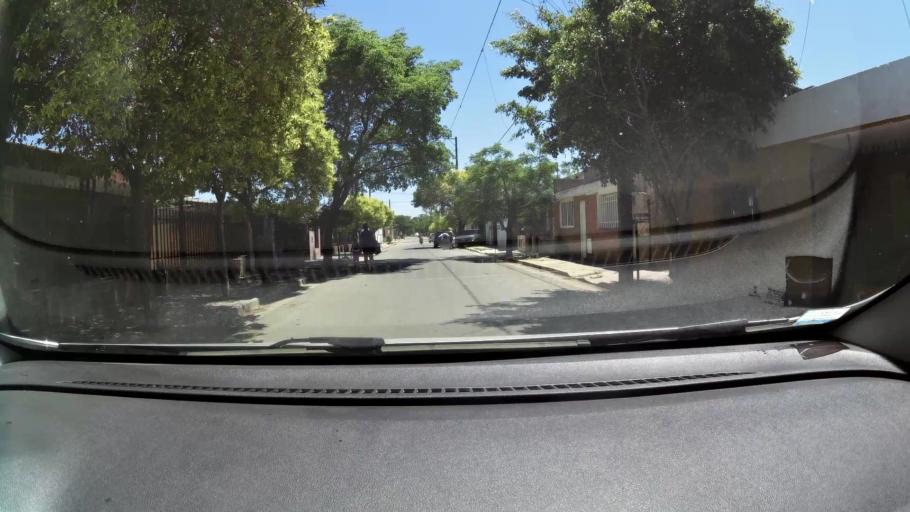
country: AR
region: Cordoba
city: Malvinas Argentinas
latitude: -31.4233
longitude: -64.1161
